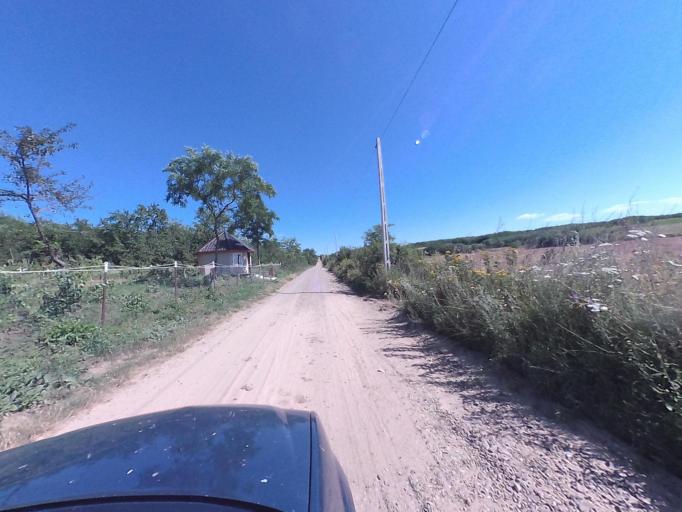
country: RO
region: Vaslui
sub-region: Comuna Costesti
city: Costesti
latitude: 46.4810
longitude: 27.7690
